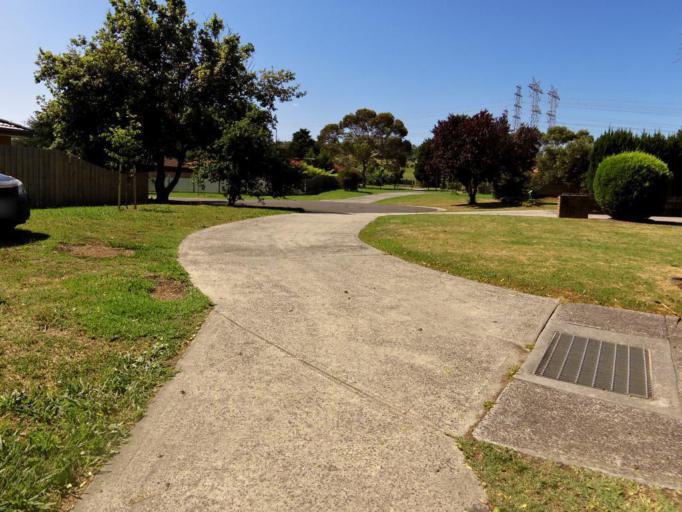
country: AU
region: Victoria
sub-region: Casey
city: Endeavour Hills
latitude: -37.9618
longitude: 145.2659
